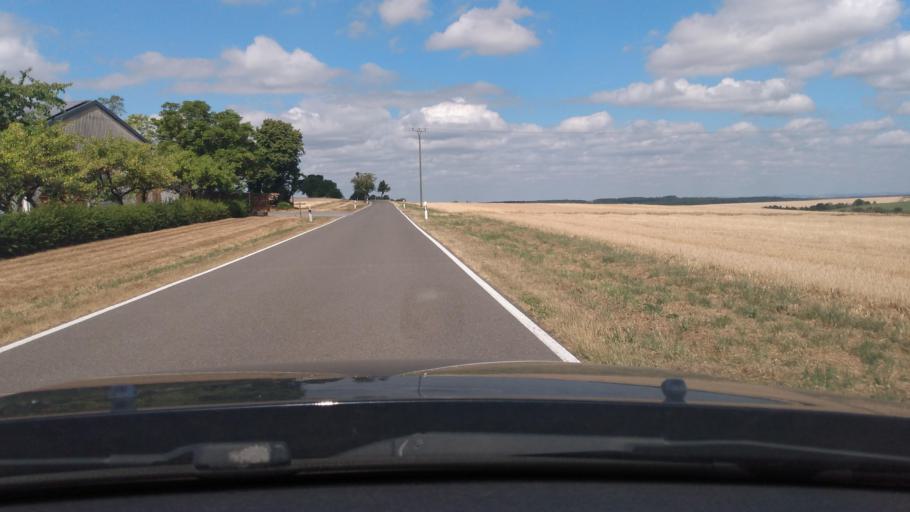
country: DE
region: Rheinland-Pfalz
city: Kleinich
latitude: 49.8976
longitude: 7.1791
